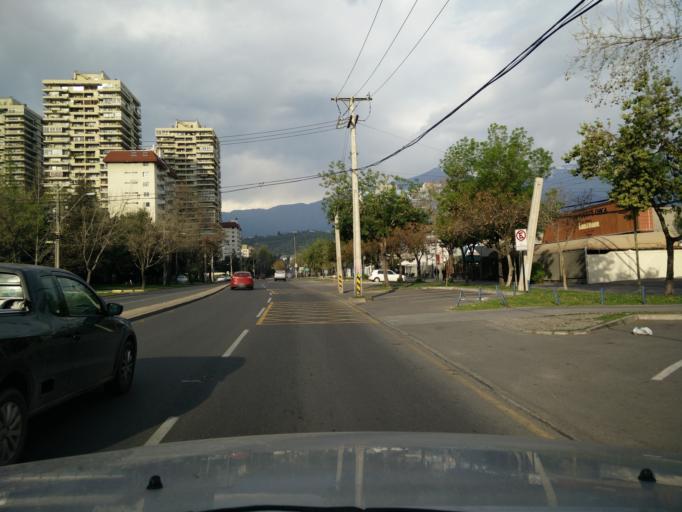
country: CL
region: Santiago Metropolitan
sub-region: Provincia de Santiago
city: Villa Presidente Frei, Nunoa, Santiago, Chile
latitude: -33.4084
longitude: -70.5512
